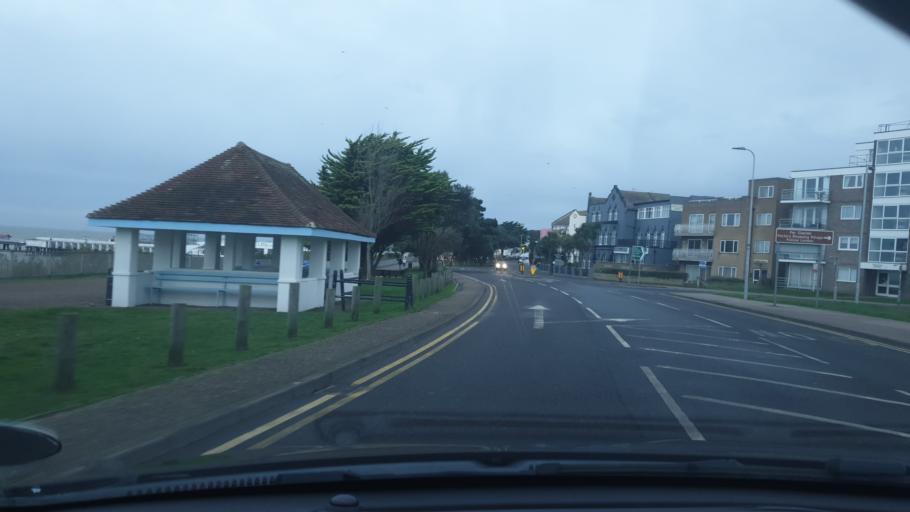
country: GB
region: England
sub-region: Essex
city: Clacton-on-Sea
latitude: 51.7890
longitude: 1.1587
